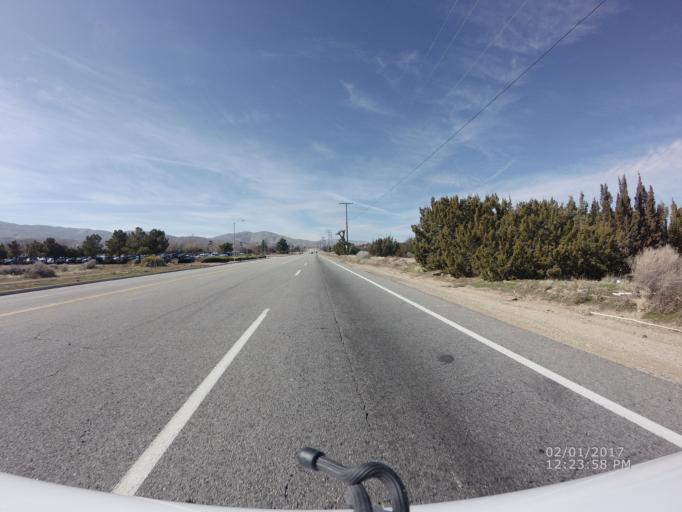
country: US
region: California
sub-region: Los Angeles County
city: Palmdale
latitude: 34.5580
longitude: -118.1377
